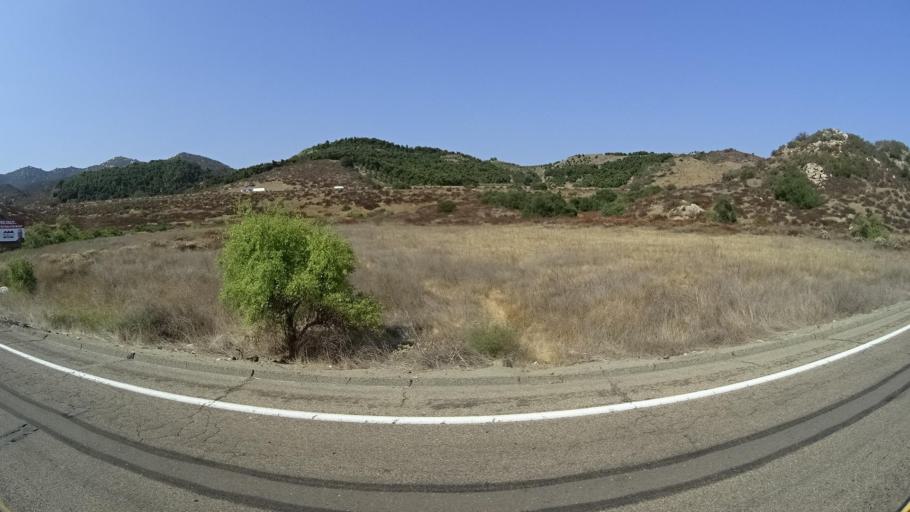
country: US
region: California
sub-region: San Diego County
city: Hidden Meadows
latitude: 33.2441
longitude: -117.1492
